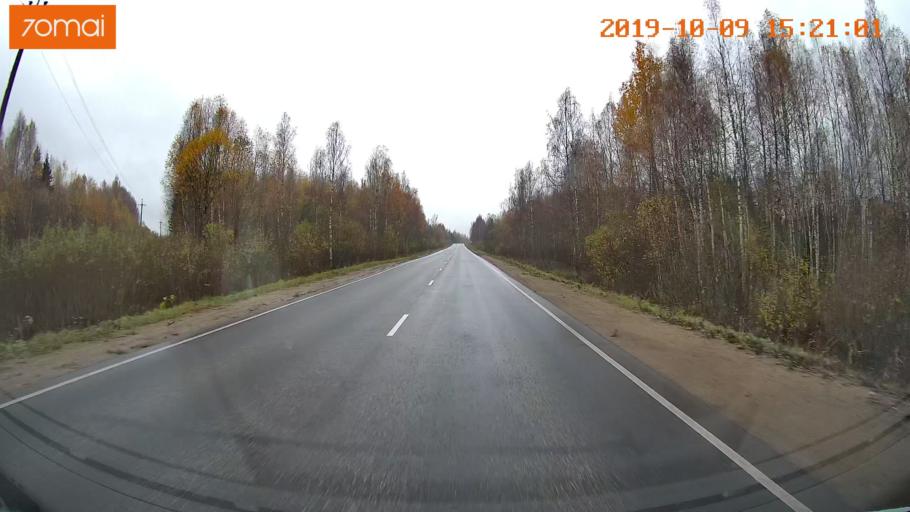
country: RU
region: Kostroma
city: Susanino
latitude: 58.0580
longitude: 41.5273
